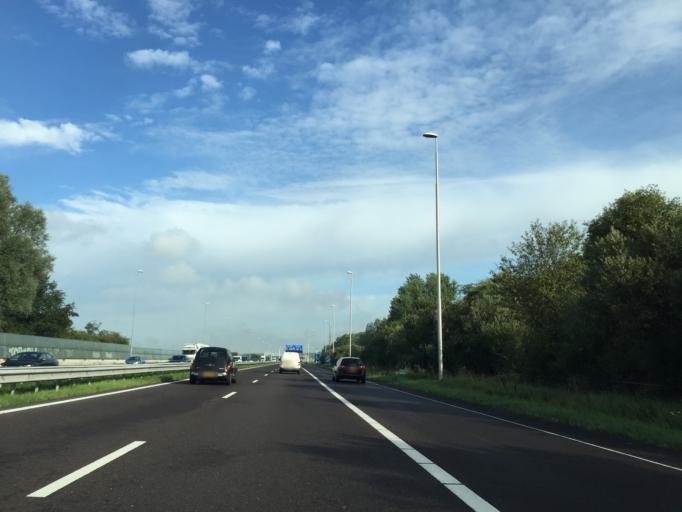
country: NL
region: North Holland
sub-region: Gemeente Velsen
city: Velsen-Zuid
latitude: 52.4304
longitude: 4.6786
